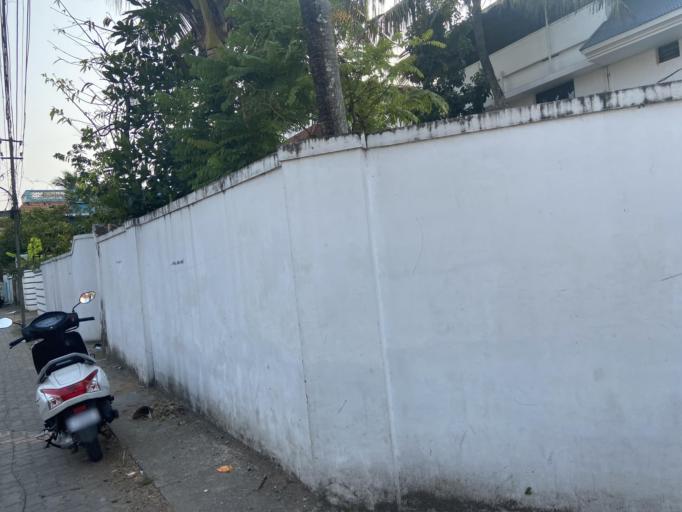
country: IN
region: Kerala
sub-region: Ernakulam
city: Cochin
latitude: 9.9485
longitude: 76.2593
